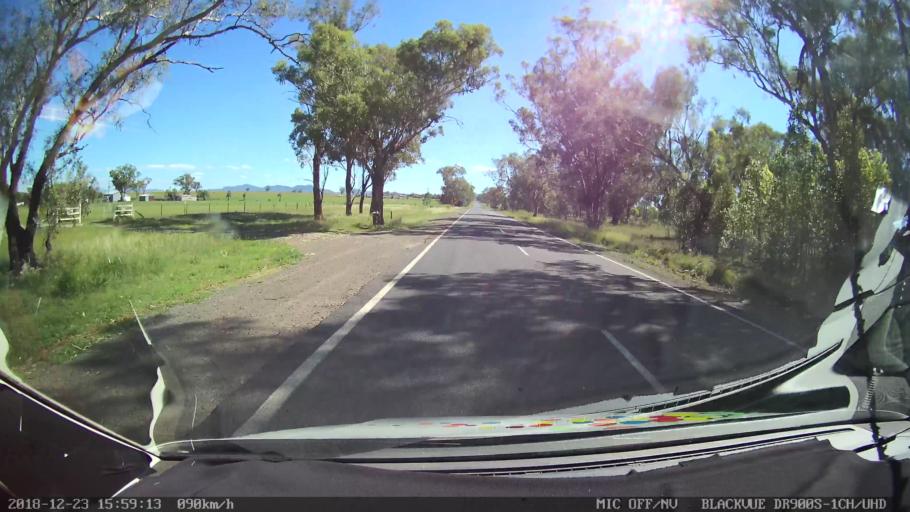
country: AU
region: New South Wales
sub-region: Tamworth Municipality
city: Phillip
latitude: -31.1972
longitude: 150.8351
